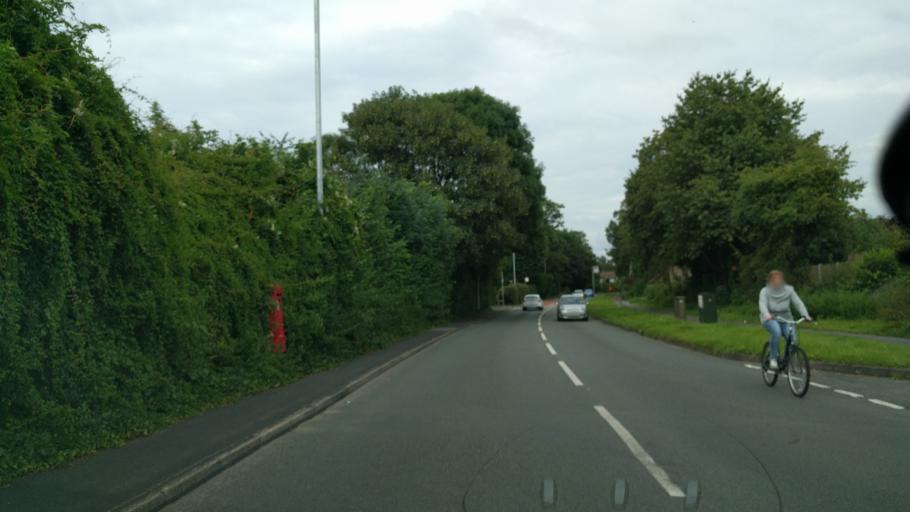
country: GB
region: England
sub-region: Warrington
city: Croft
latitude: 53.4159
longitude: -2.5639
